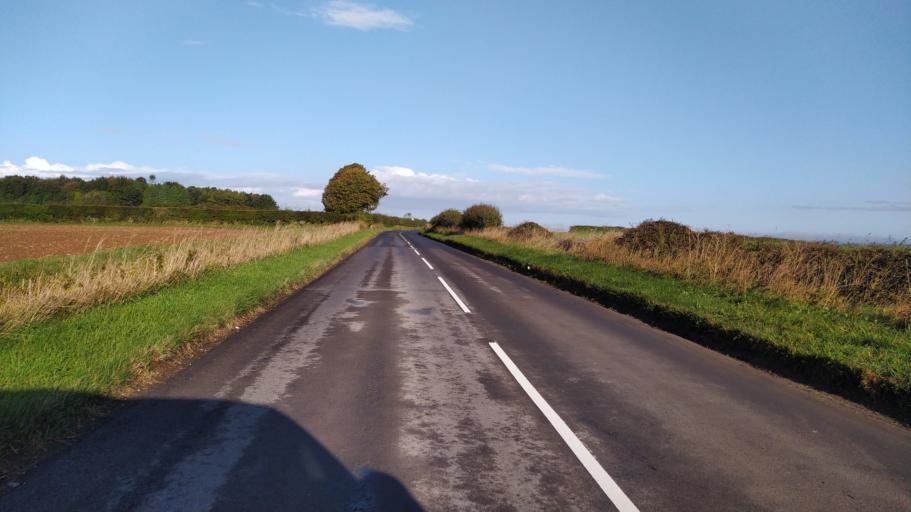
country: GB
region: England
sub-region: Dorset
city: Wimborne Minster
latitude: 50.8877
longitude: -2.0012
